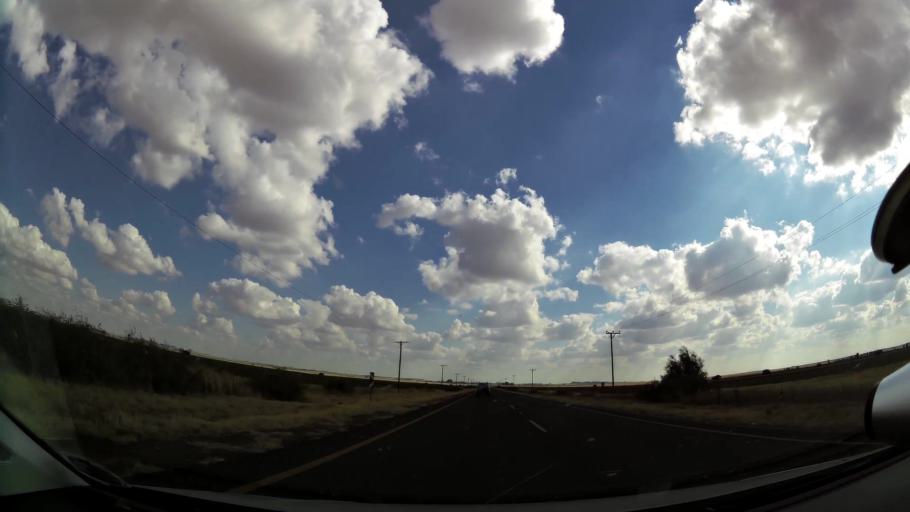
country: ZA
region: Orange Free State
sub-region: Xhariep District Municipality
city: Koffiefontein
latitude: -29.1310
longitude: 25.5245
